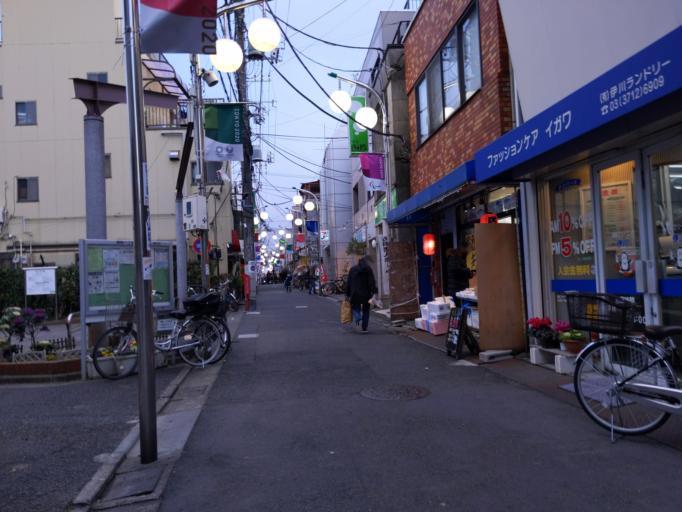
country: JP
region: Tokyo
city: Tokyo
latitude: 35.6167
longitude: 139.6968
